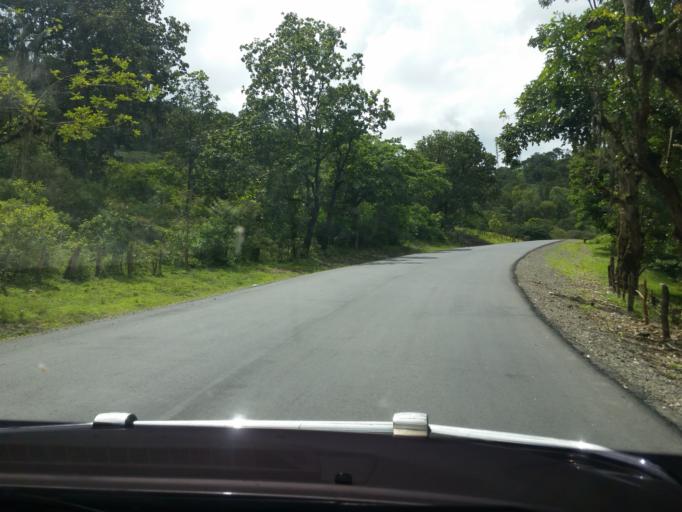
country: NI
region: Jinotega
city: Jinotega
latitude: 13.1516
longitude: -85.9471
